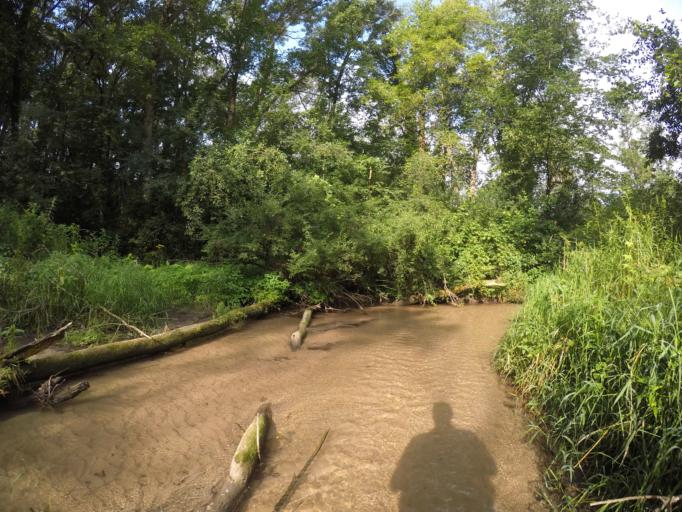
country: US
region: Minnesota
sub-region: Olmsted County
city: Eyota
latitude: 43.9805
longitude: -92.3382
